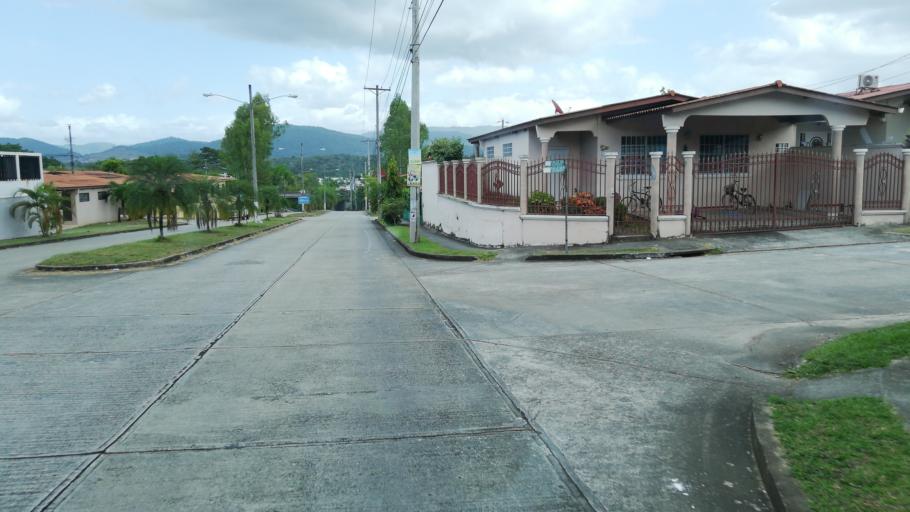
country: PA
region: Panama
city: San Miguelito
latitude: 9.0774
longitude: -79.4573
